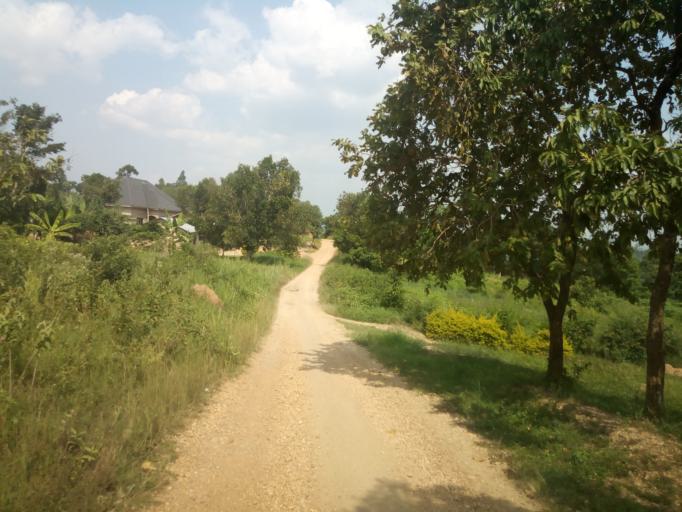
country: UG
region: Western Region
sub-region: Kanungu District
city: Ntungamo
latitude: -0.7935
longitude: 29.6620
